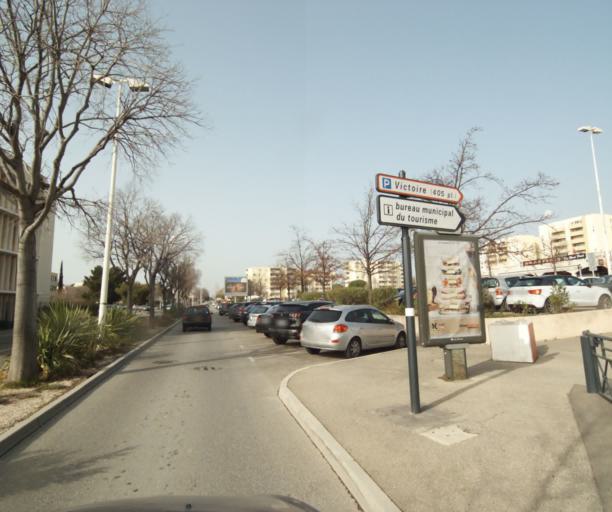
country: FR
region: Provence-Alpes-Cote d'Azur
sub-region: Departement des Bouches-du-Rhone
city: Vitrolles
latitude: 43.4473
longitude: 5.2474
